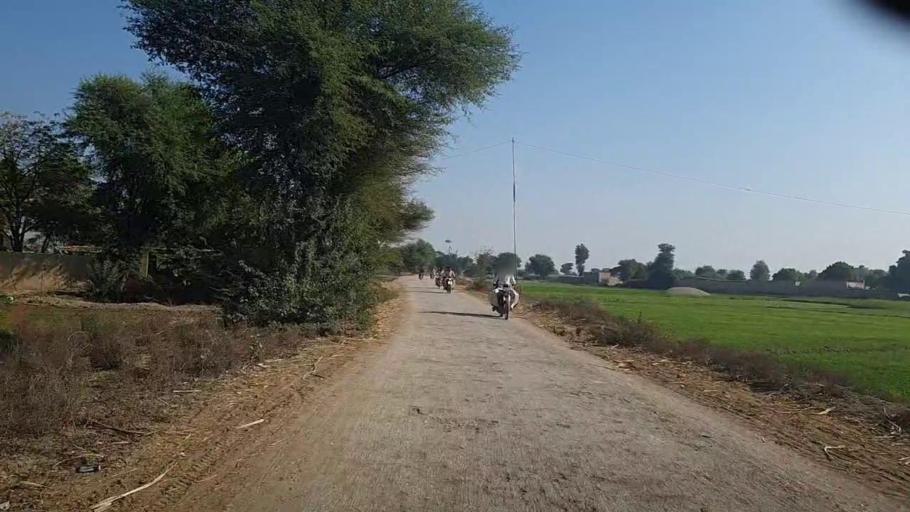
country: PK
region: Sindh
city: Darya Khan Marri
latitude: 26.6587
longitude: 68.3459
